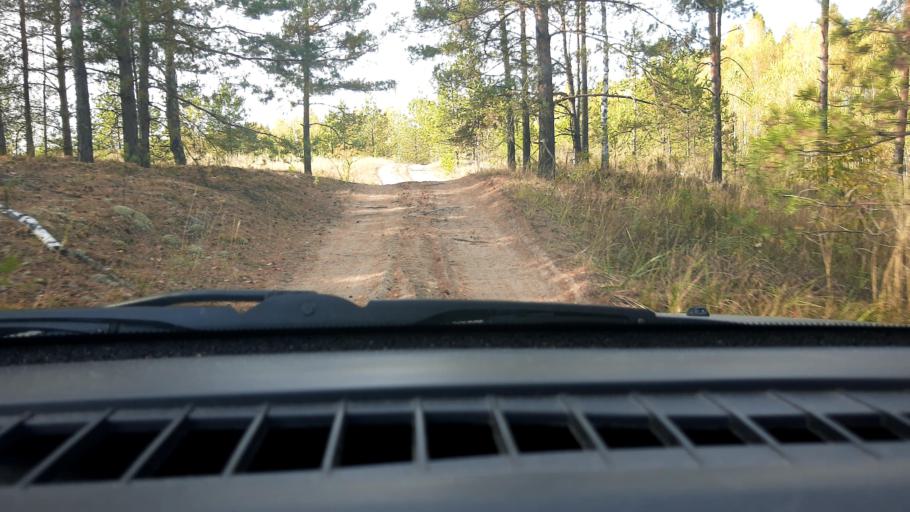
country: RU
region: Nizjnij Novgorod
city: Lukino
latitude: 56.3906
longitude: 43.5901
